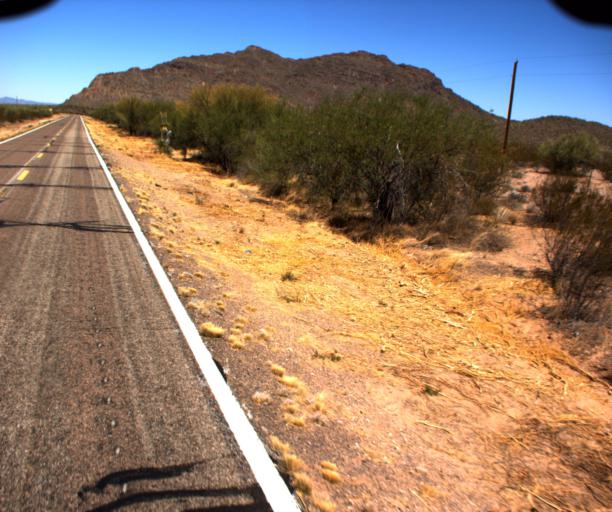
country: US
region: Arizona
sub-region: Pima County
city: Ajo
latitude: 32.2225
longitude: -112.6718
